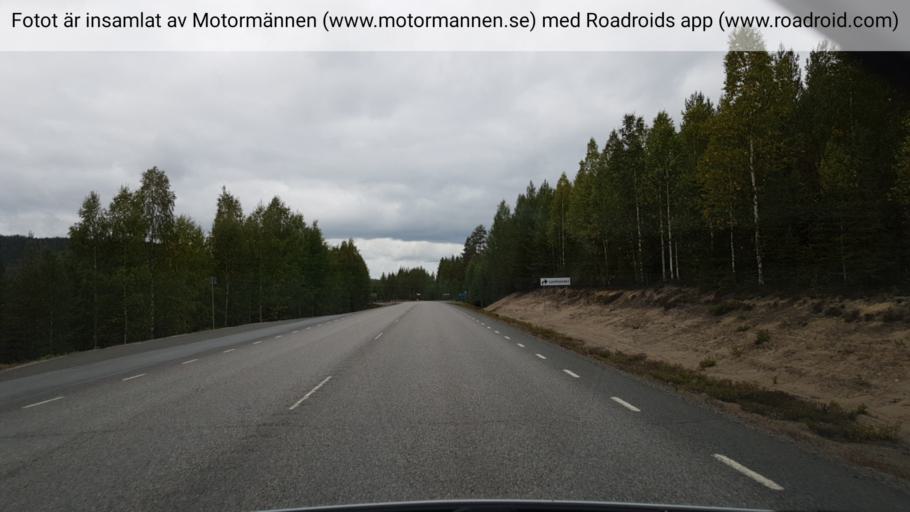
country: SE
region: Vaesterbotten
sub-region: Skelleftea Kommun
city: Langsele
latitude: 64.9189
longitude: 20.0870
